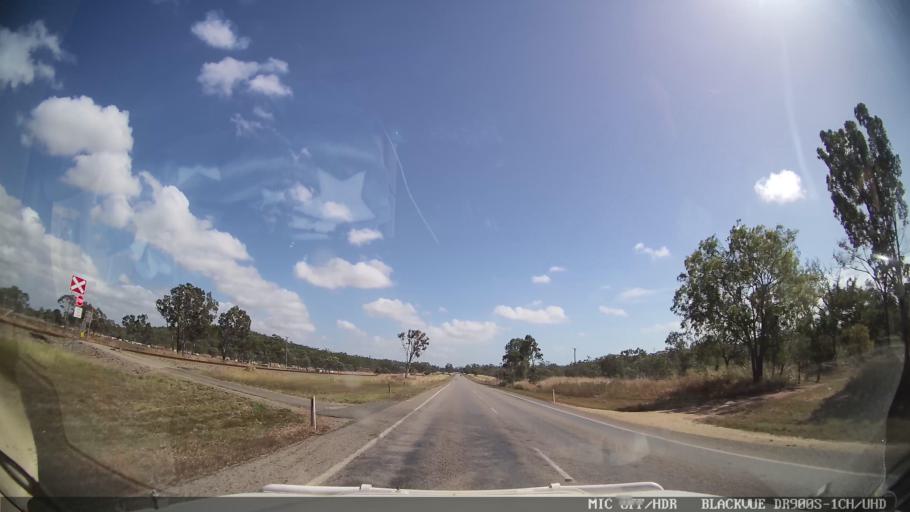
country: AU
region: Queensland
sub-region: Whitsunday
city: Red Hill
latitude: -20.1837
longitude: 148.3537
